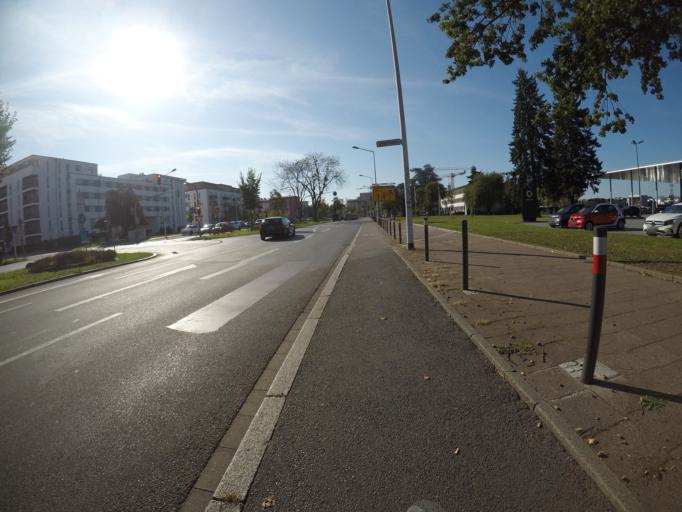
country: DE
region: Hesse
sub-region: Regierungsbezirk Darmstadt
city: Darmstadt
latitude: 49.8697
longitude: 8.6331
